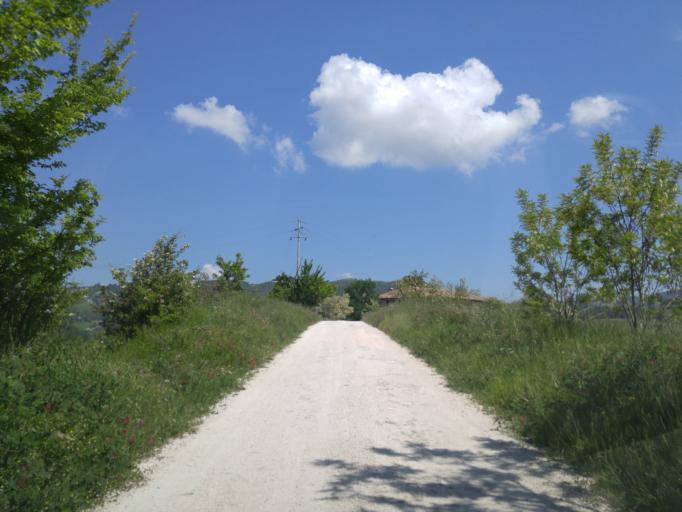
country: IT
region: The Marches
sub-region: Provincia di Pesaro e Urbino
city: Fermignano
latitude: 43.7013
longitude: 12.6521
